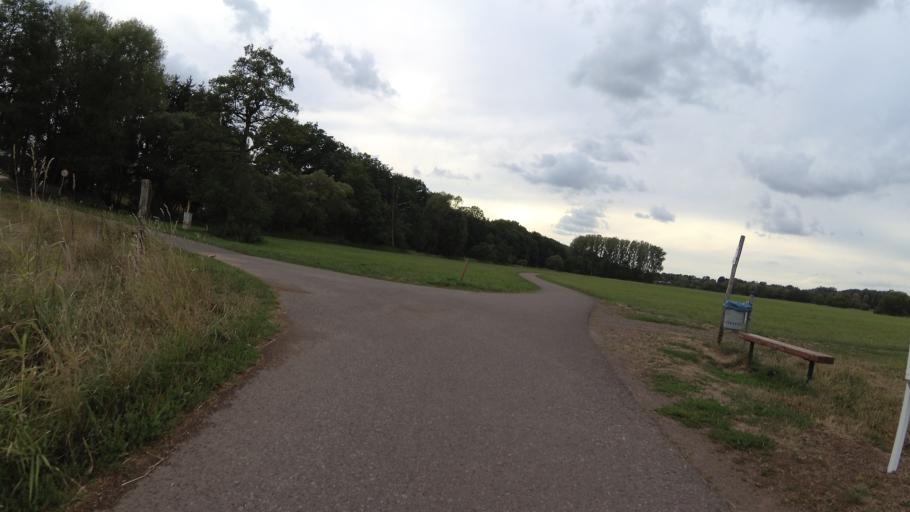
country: DE
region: Saarland
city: Homburg
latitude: 49.3100
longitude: 7.2953
